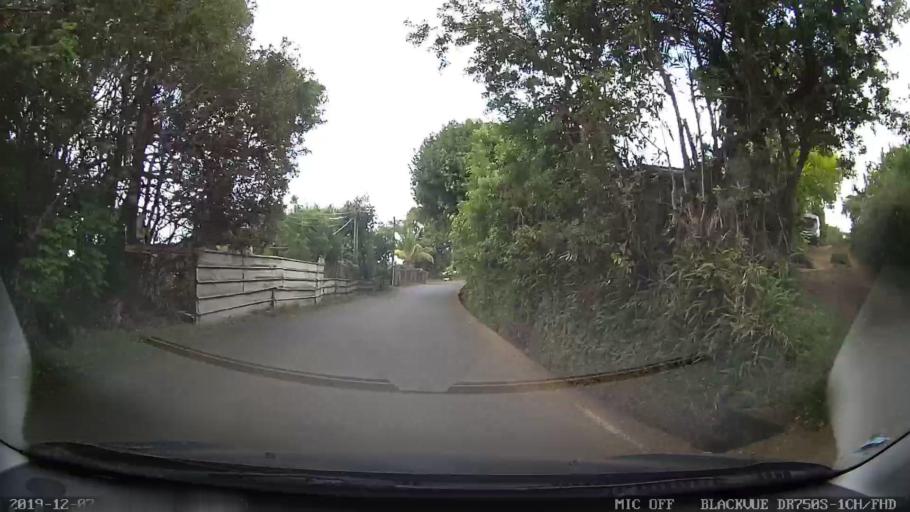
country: RE
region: Reunion
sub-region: Reunion
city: Sainte-Marie
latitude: -20.9366
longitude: 55.5340
